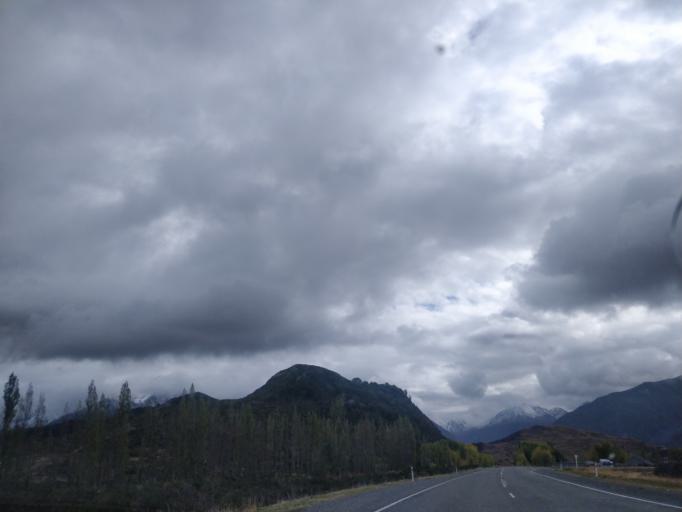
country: NZ
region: Canterbury
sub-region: Waimakariri District
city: Oxford
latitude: -43.0309
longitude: 171.7475
